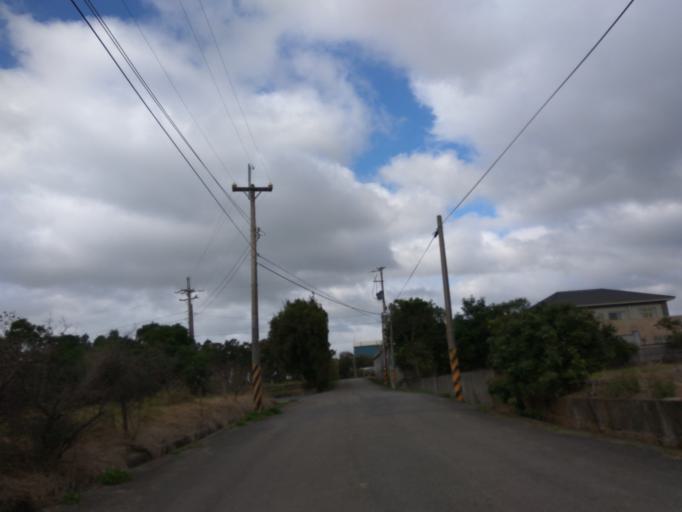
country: TW
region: Taiwan
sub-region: Hsinchu
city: Zhubei
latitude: 24.9724
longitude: 121.0863
